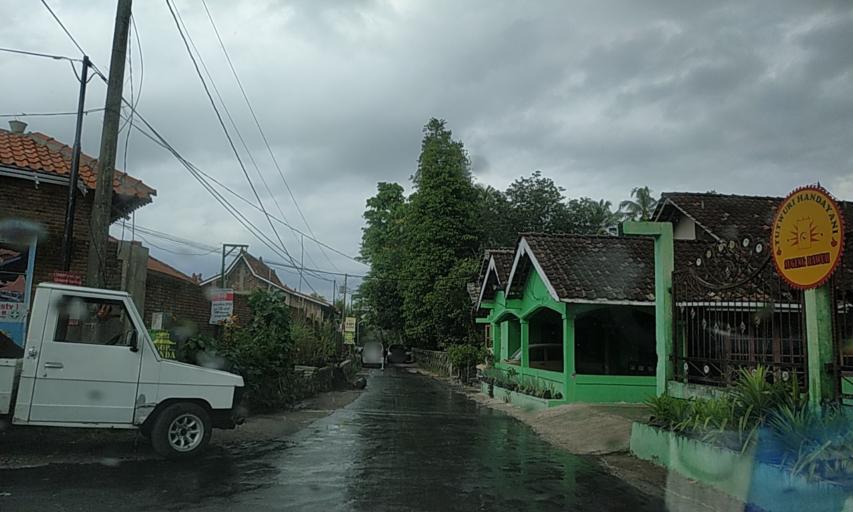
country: ID
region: Daerah Istimewa Yogyakarta
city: Sleman
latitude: -7.6706
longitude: 110.4205
